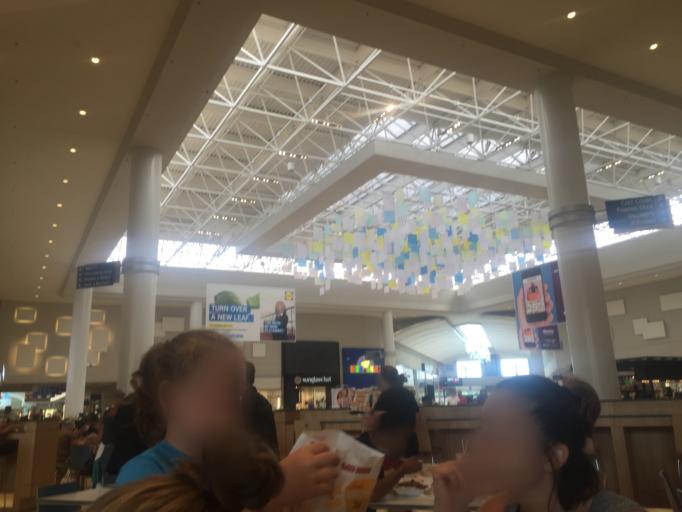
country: US
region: Virginia
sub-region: City of Virginia Beach
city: Virginia Beach
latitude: 36.8160
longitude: -76.0719
